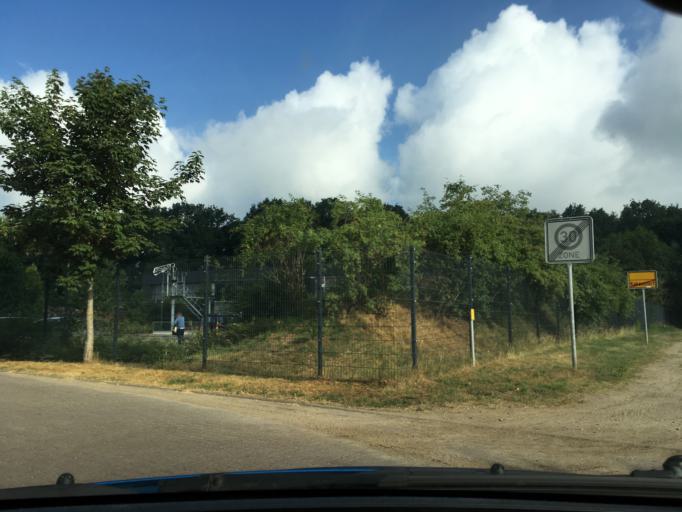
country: DE
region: Lower Saxony
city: Kakenstorf
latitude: 53.3133
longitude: 9.7713
